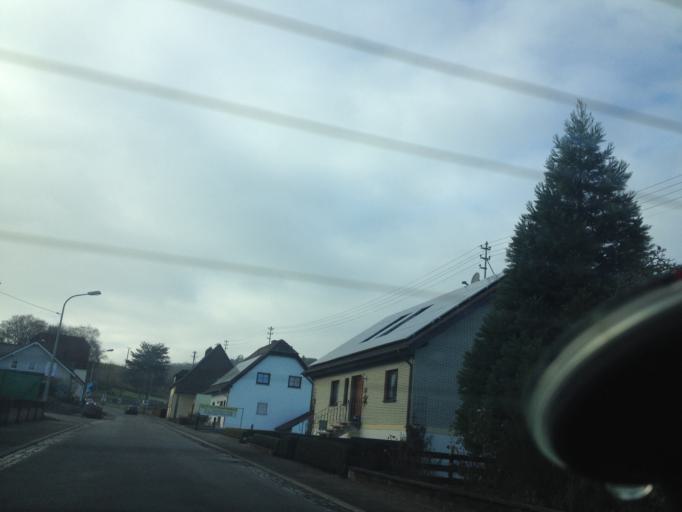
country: DE
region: Rheinland-Pfalz
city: Borsborn
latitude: 49.4523
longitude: 7.3796
